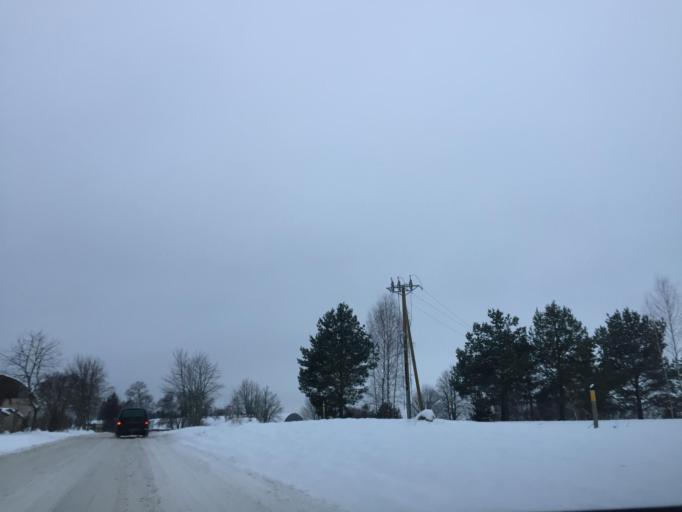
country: LV
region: Smiltene
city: Smiltene
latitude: 57.4295
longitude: 25.9132
